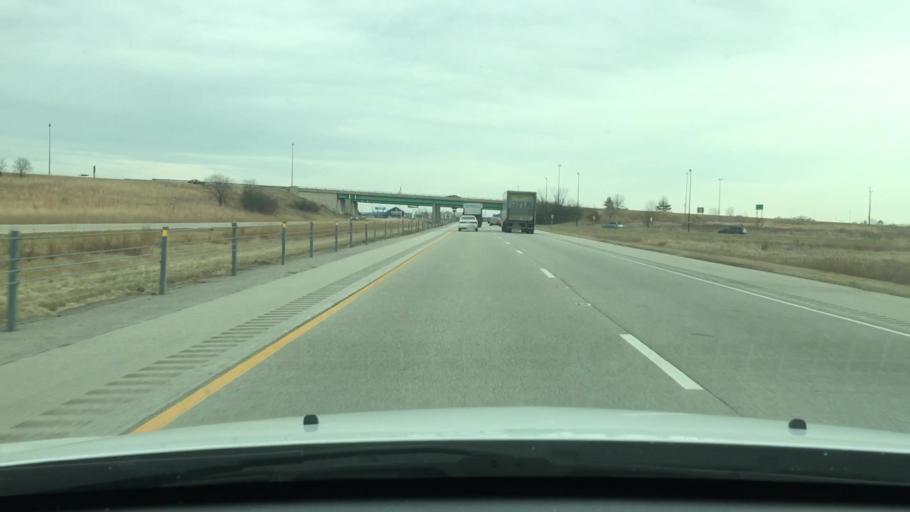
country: US
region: Illinois
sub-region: Sangamon County
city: Jerome
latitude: 39.7434
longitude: -89.7091
